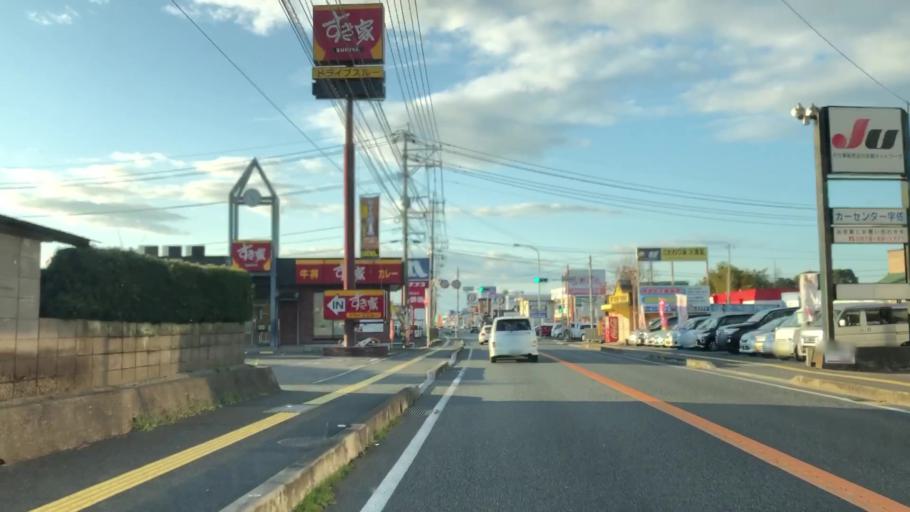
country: JP
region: Oita
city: Bungo-Takada-shi
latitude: 33.5299
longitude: 131.3369
